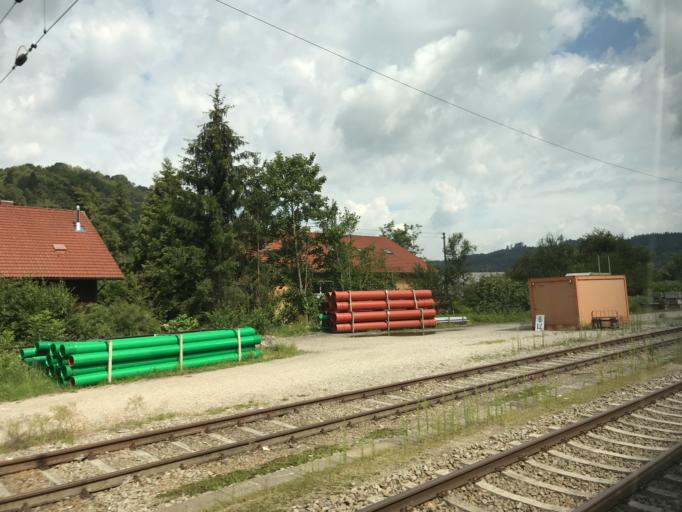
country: AT
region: Upper Austria
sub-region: Politischer Bezirk Scharding
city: Scharding
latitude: 48.5053
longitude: 13.4563
